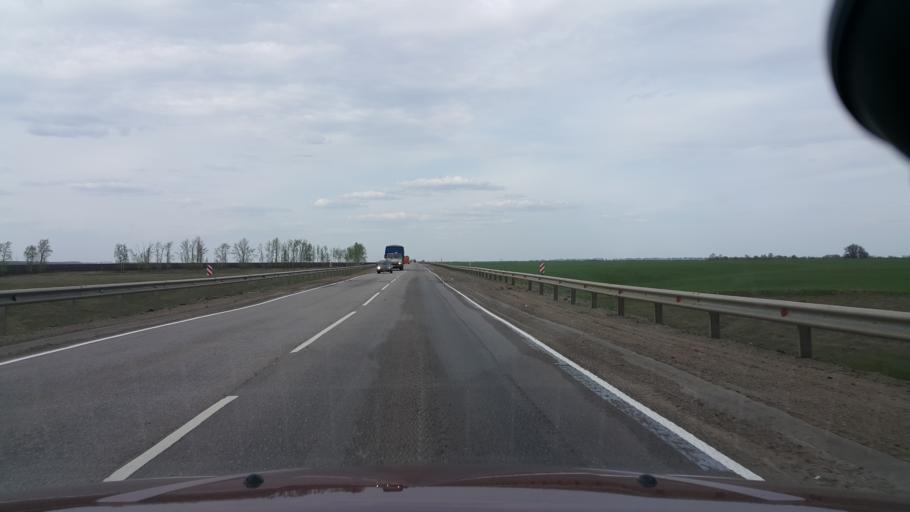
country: RU
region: Tambov
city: Pokrovo-Prigorodnoye
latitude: 52.6123
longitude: 41.3439
